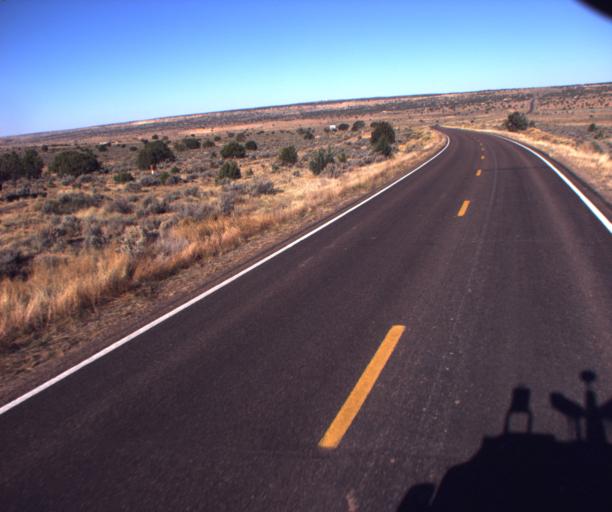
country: US
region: Arizona
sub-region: Navajo County
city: First Mesa
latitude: 35.7480
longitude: -110.1252
